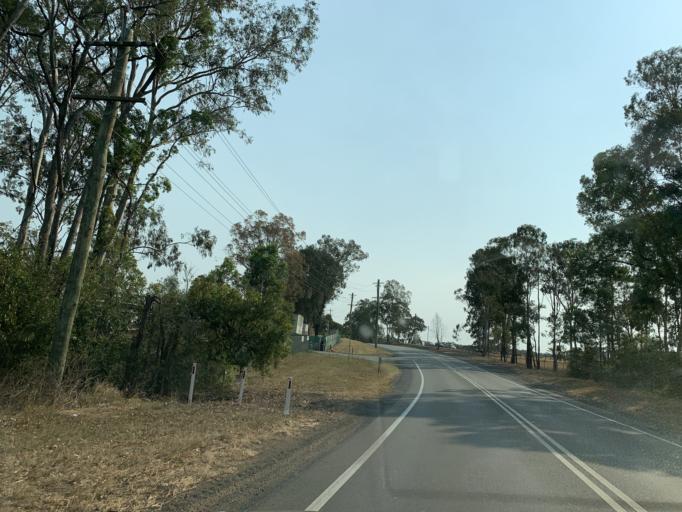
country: AU
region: New South Wales
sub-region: Blacktown
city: Rouse Hill
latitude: -33.6630
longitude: 150.9211
